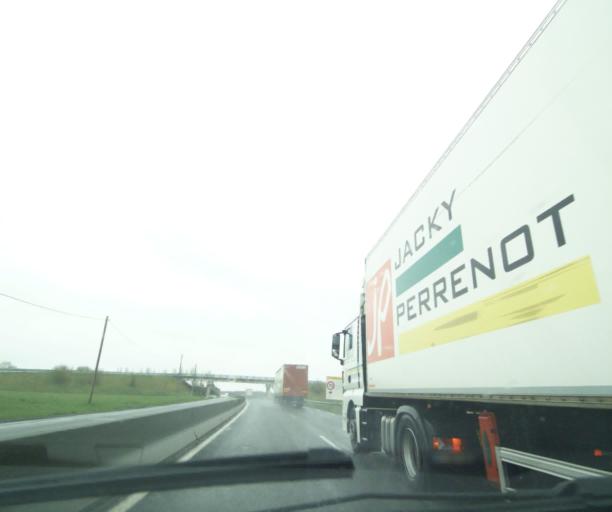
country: FR
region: Ile-de-France
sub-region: Departement de l'Essonne
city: Etampes
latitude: 48.4032
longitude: 2.1218
